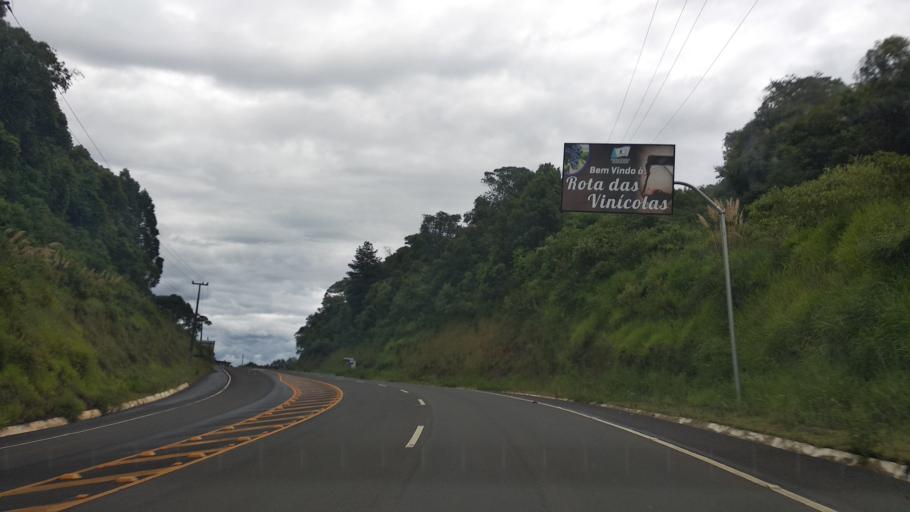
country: BR
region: Santa Catarina
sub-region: Videira
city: Videira
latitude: -27.0518
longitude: -51.1791
